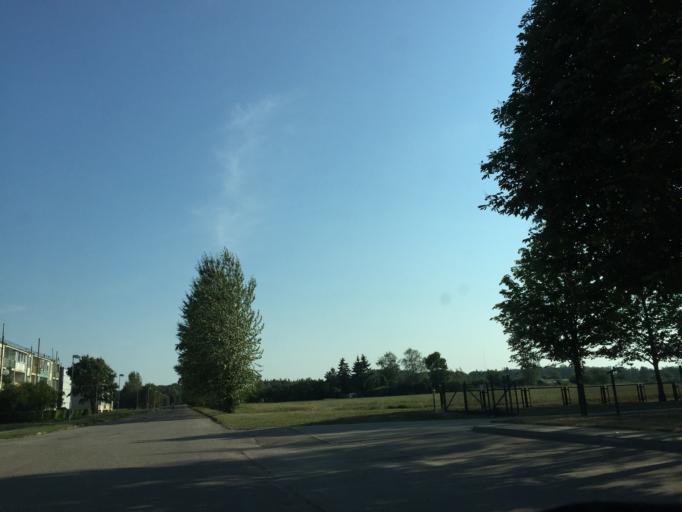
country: LT
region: Siauliu apskritis
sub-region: Joniskis
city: Joniskis
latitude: 56.4188
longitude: 23.6985
